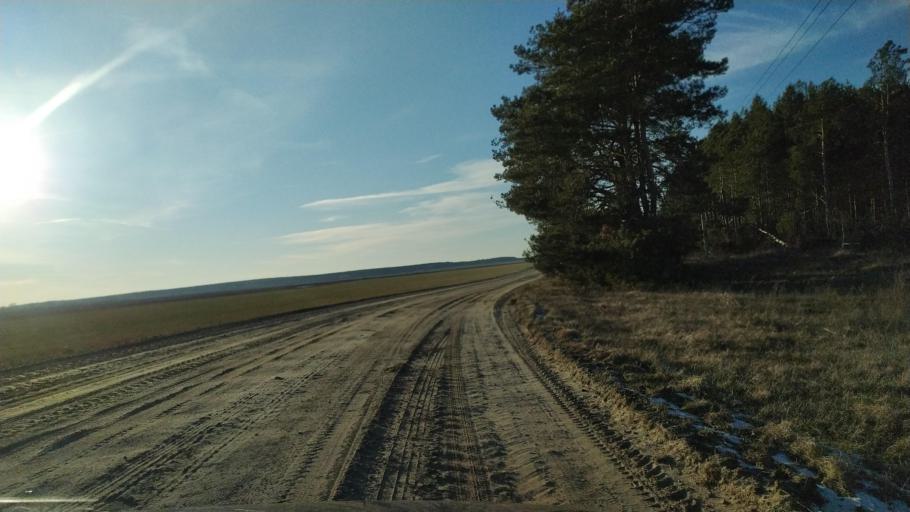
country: BY
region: Brest
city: Pruzhany
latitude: 52.5455
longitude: 24.2833
